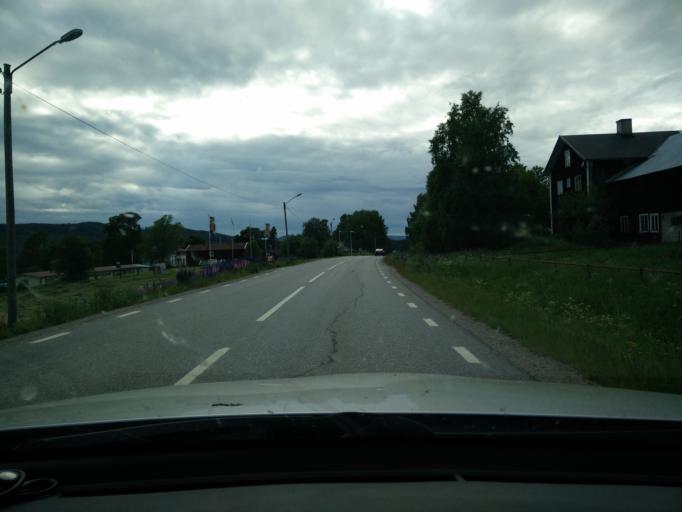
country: SE
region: Gaevleborg
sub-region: Hudiksvalls Kommun
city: Delsbo
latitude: 62.0995
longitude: 16.7343
